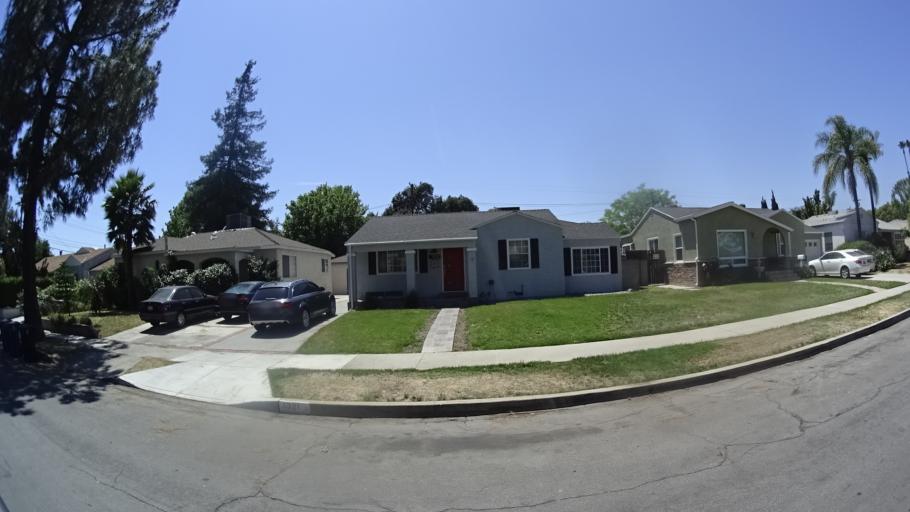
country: US
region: California
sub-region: Los Angeles County
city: Burbank
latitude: 34.1780
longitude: -118.3428
